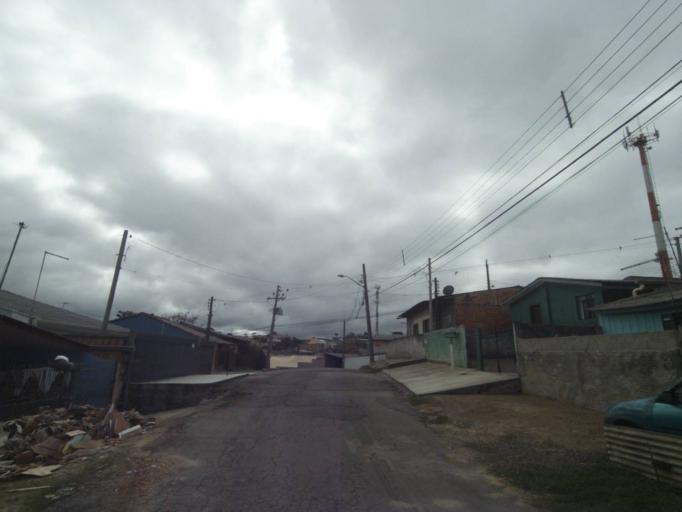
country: BR
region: Parana
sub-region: Sao Jose Dos Pinhais
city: Sao Jose dos Pinhais
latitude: -25.5384
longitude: -49.3004
